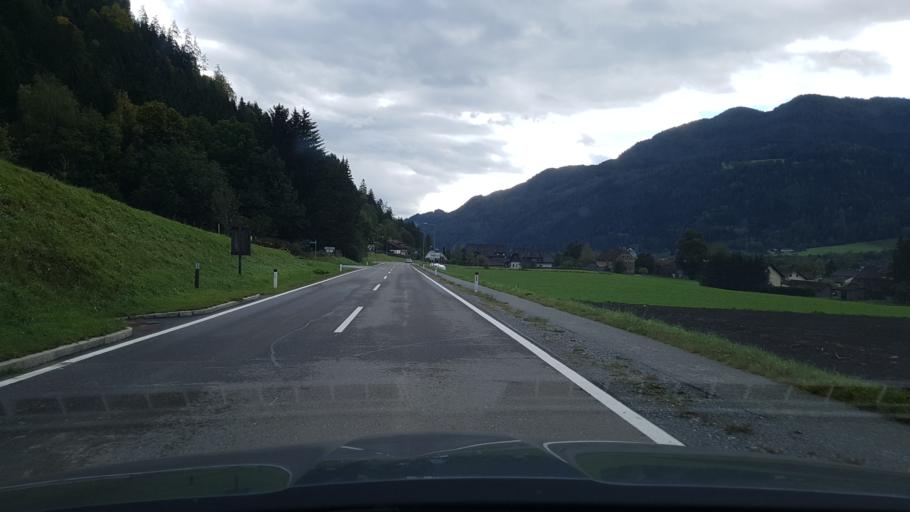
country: AT
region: Styria
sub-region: Politischer Bezirk Murau
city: Triebendorf
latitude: 47.1461
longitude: 14.2803
